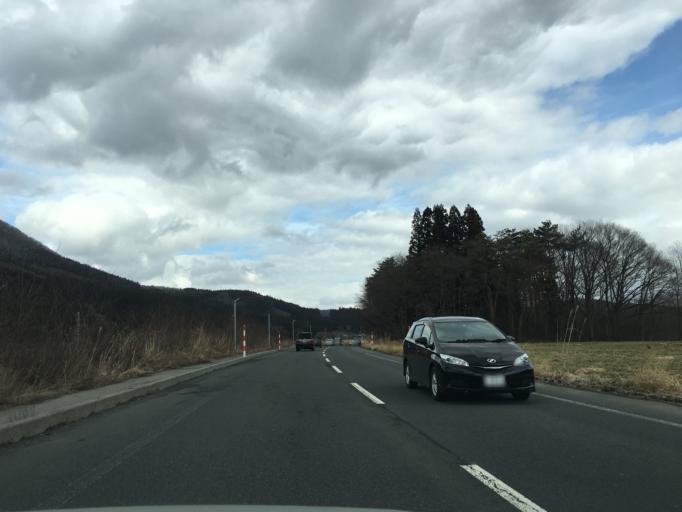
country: JP
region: Akita
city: Hanawa
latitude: 40.2299
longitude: 140.6815
